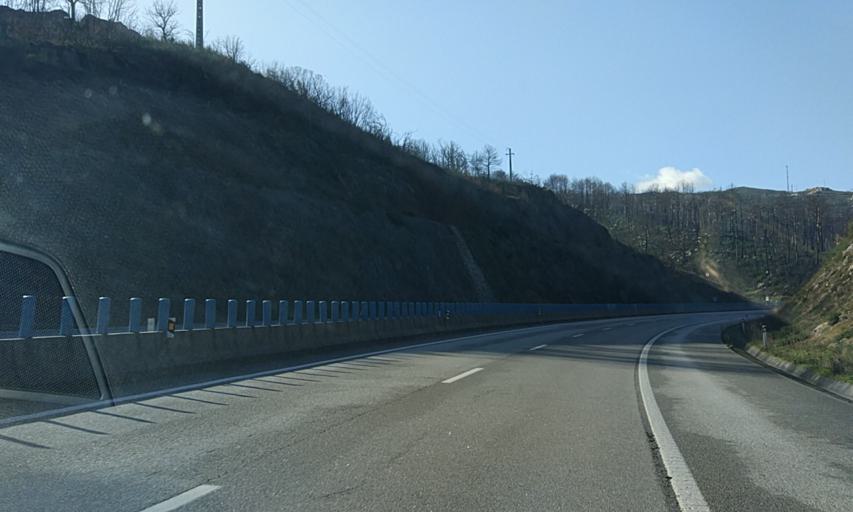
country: PT
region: Viseu
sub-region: Vouzela
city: Vouzela
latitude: 40.6972
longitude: -8.0941
